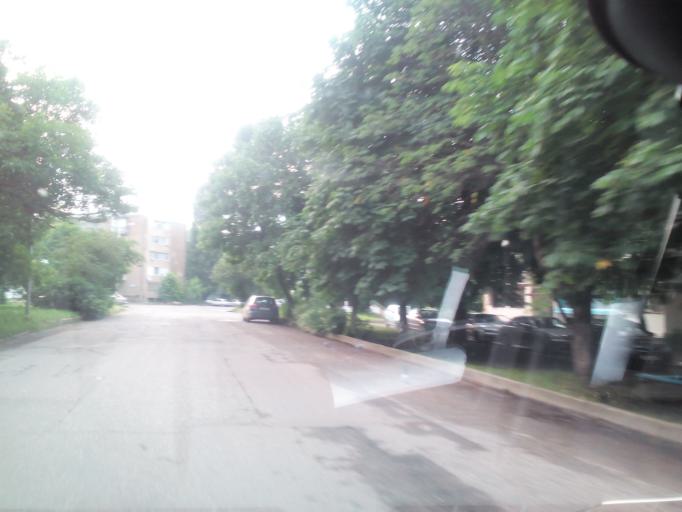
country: RU
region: Stavropol'skiy
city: Pyatigorsk
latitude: 44.0491
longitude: 43.0420
